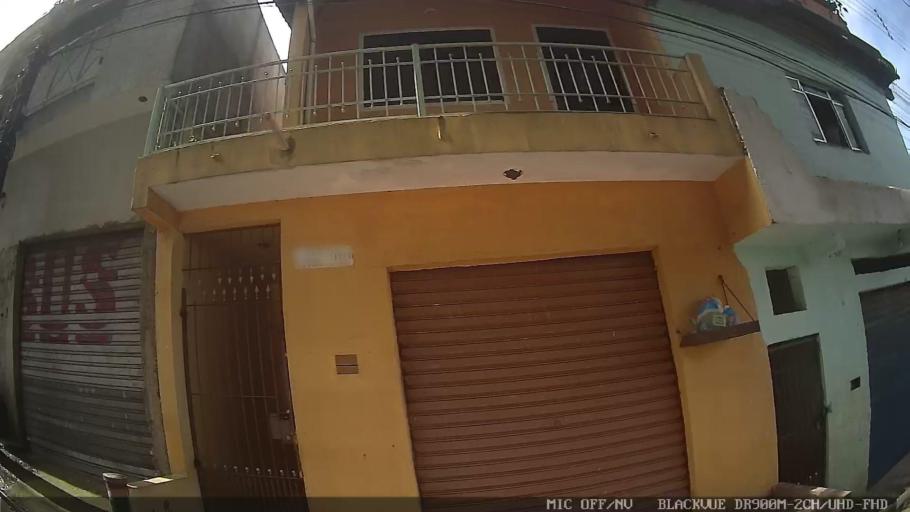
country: BR
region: Sao Paulo
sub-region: Itaquaquecetuba
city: Itaquaquecetuba
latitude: -23.4713
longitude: -46.3045
